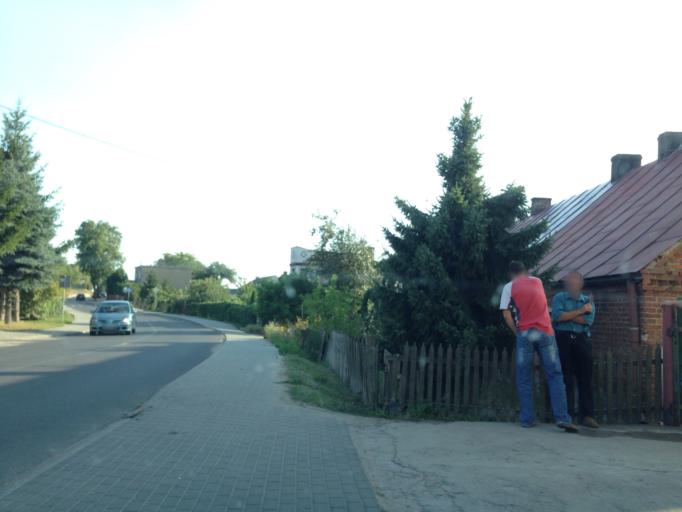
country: PL
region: Kujawsko-Pomorskie
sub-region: Powiat brodnicki
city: Brodnica
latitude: 53.3321
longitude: 19.3747
